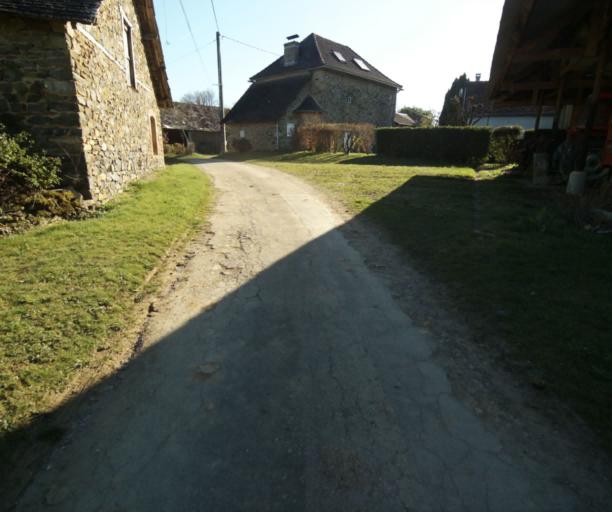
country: FR
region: Limousin
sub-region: Departement de la Correze
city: Seilhac
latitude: 45.3853
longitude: 1.7347
